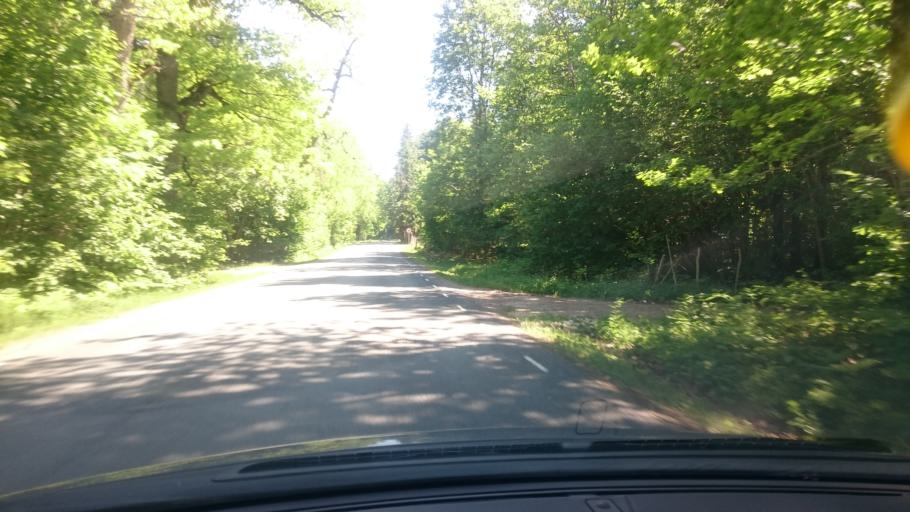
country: EE
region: Harju
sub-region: Rae vald
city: Vaida
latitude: 59.2057
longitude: 24.9265
